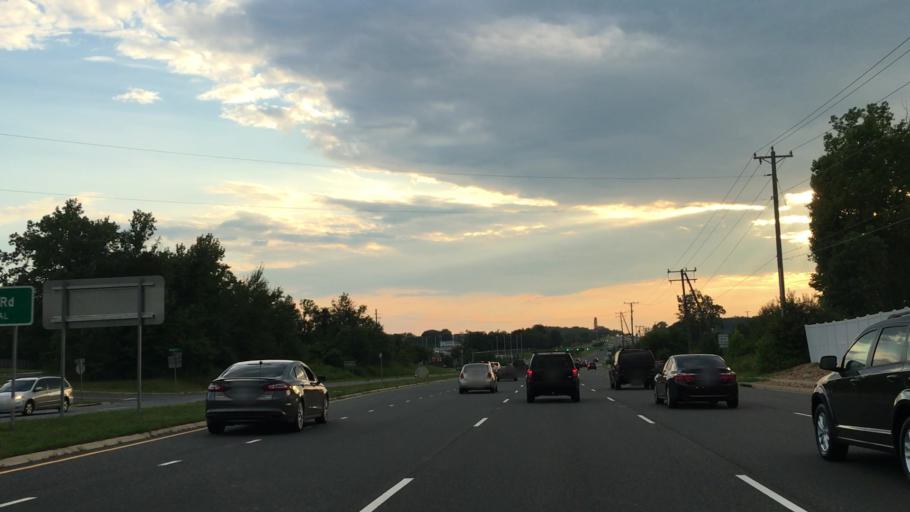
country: US
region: Virginia
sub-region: Stafford County
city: Falmouth
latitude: 38.2906
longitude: -77.5570
